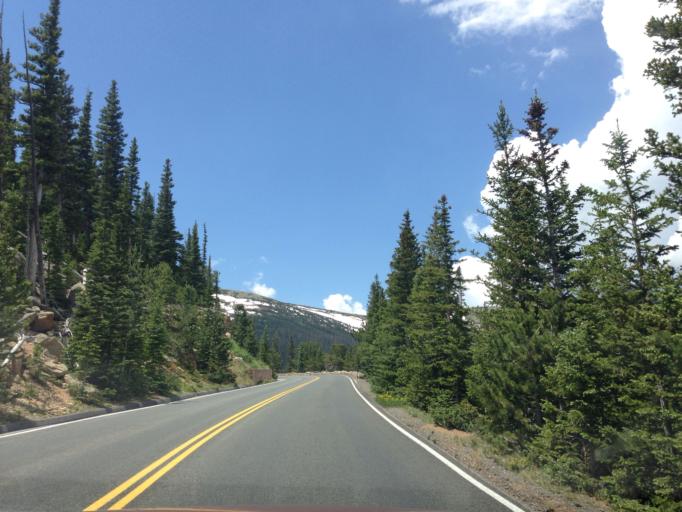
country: US
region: Colorado
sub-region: Larimer County
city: Estes Park
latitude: 40.3905
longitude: -105.6505
